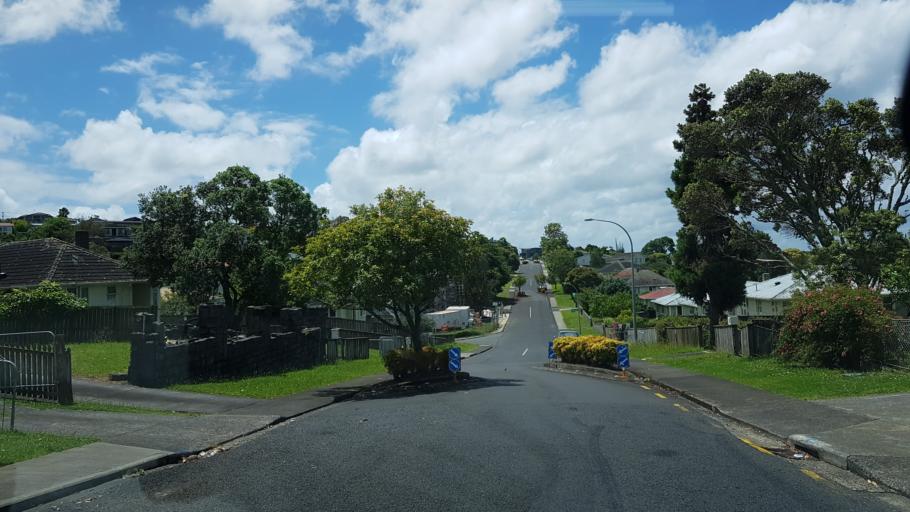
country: NZ
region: Auckland
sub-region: Auckland
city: North Shore
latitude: -36.8014
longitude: 174.7417
